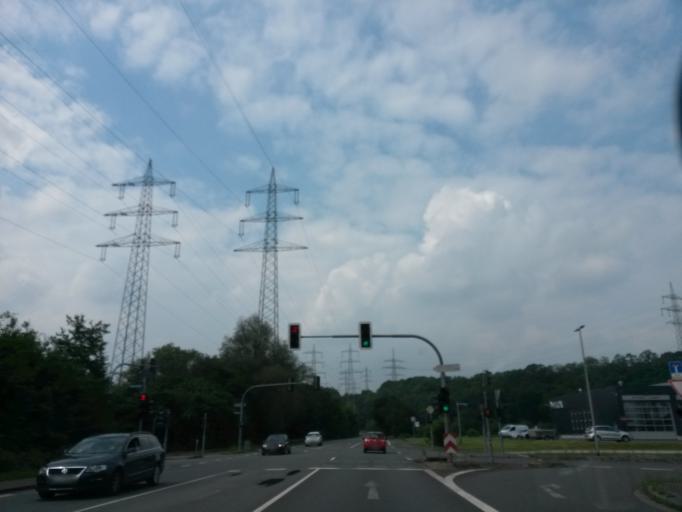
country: DE
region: North Rhine-Westphalia
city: Schwerte
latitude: 51.3772
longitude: 7.5418
